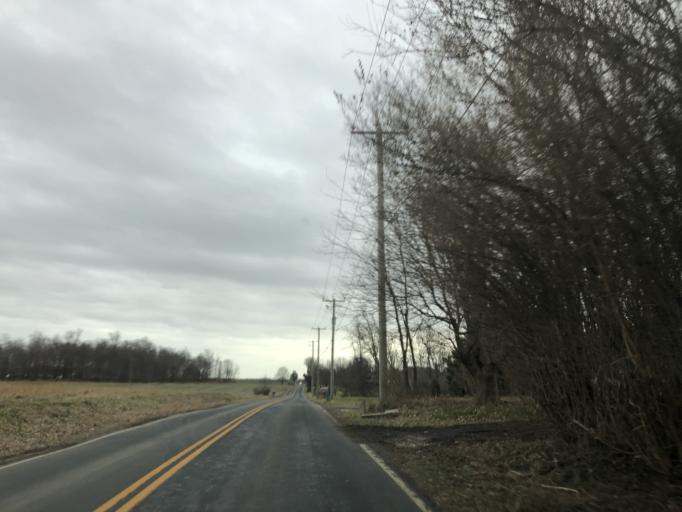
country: US
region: Pennsylvania
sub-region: Chester County
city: Oxford
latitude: 39.6979
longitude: -75.9526
